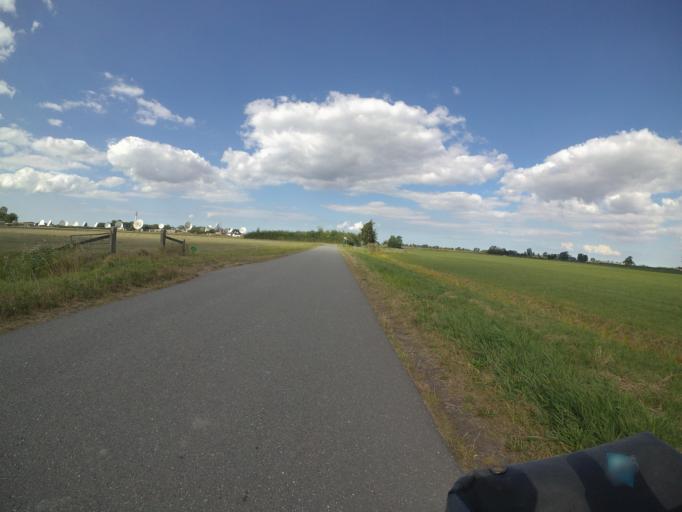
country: NL
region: Friesland
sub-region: Gemeente Kollumerland en Nieuwkruisland
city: Kollum
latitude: 53.2807
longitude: 6.2218
